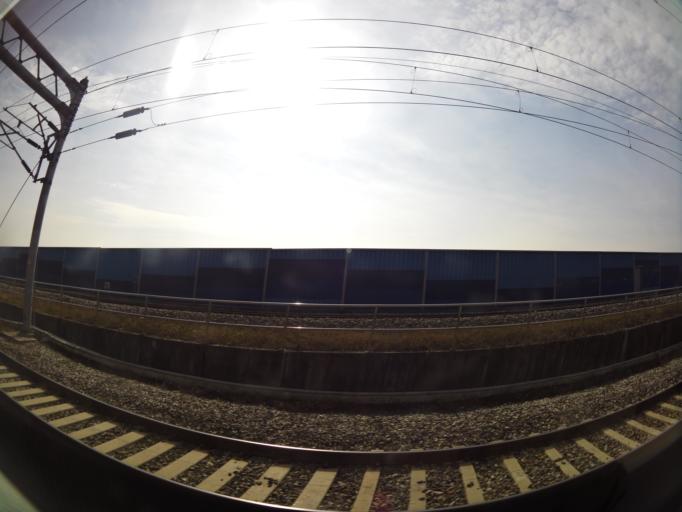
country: KR
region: Daejeon
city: Songgang-dong
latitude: 36.5337
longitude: 127.3590
